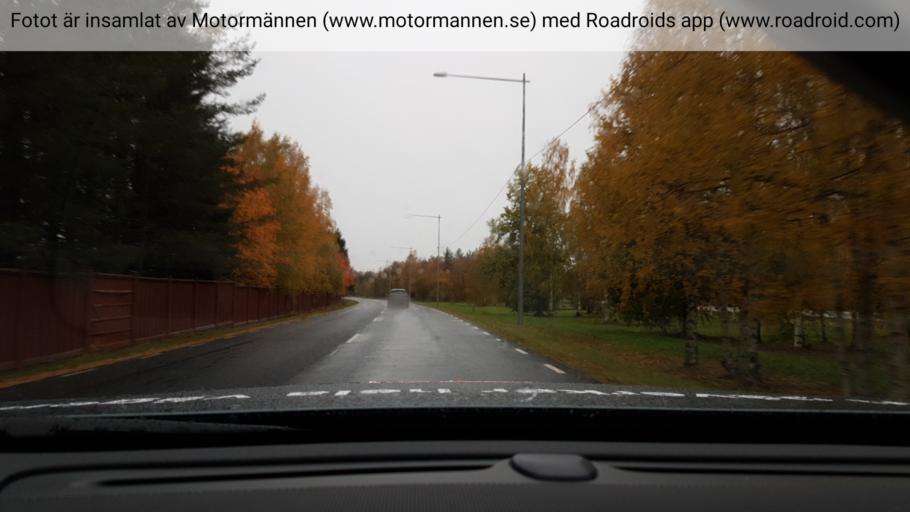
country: SE
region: Norrbotten
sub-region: Lulea Kommun
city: Gammelstad
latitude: 65.6513
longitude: 21.9881
